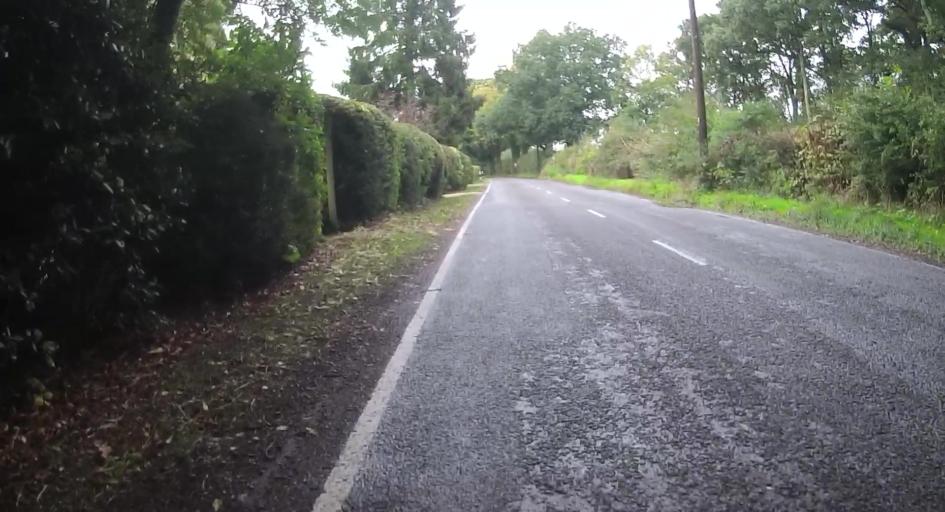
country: GB
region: England
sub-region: Hampshire
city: Tadley
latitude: 51.3468
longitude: -1.1639
